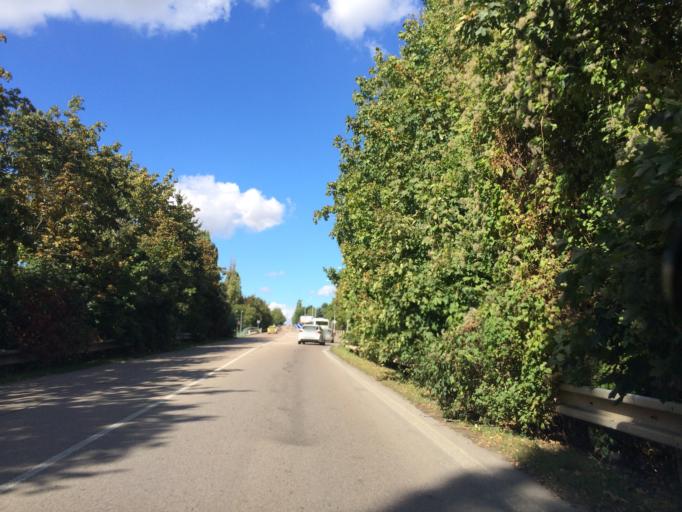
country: CZ
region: Central Bohemia
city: Hostivice
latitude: 50.0862
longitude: 14.3069
